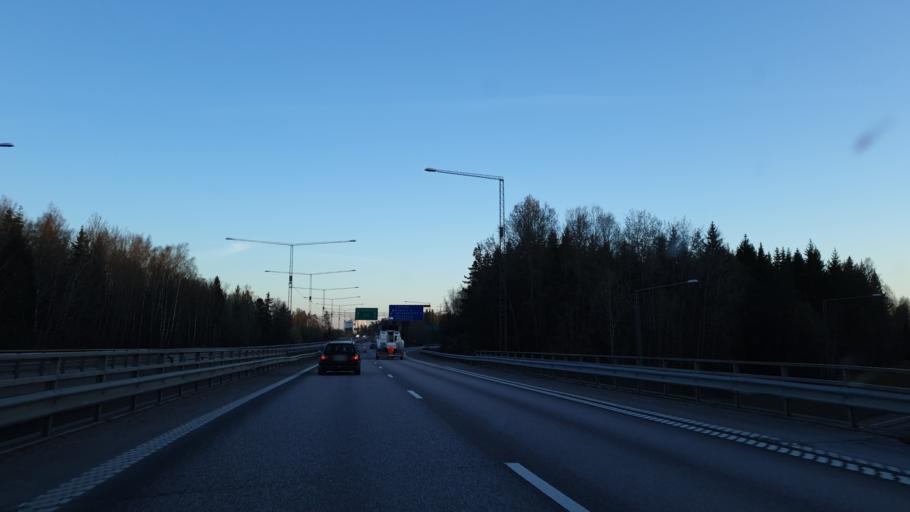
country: SE
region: Stockholm
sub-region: Sigtuna Kommun
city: Rosersberg
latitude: 59.6195
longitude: 17.9007
